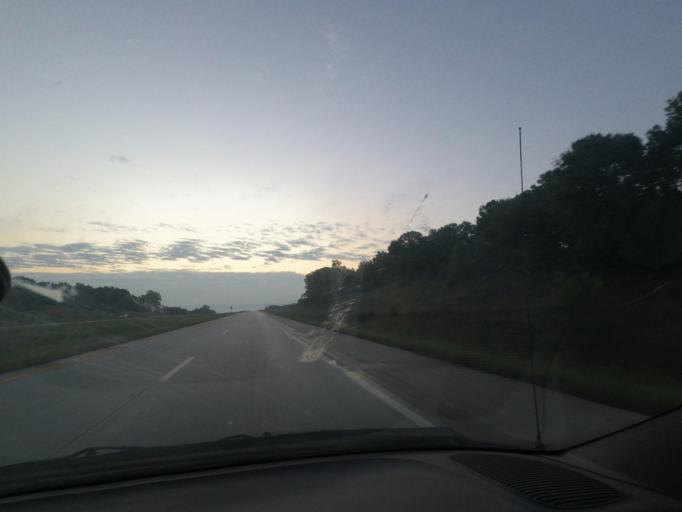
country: US
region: Missouri
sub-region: Linn County
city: Marceline
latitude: 39.7591
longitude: -92.8316
